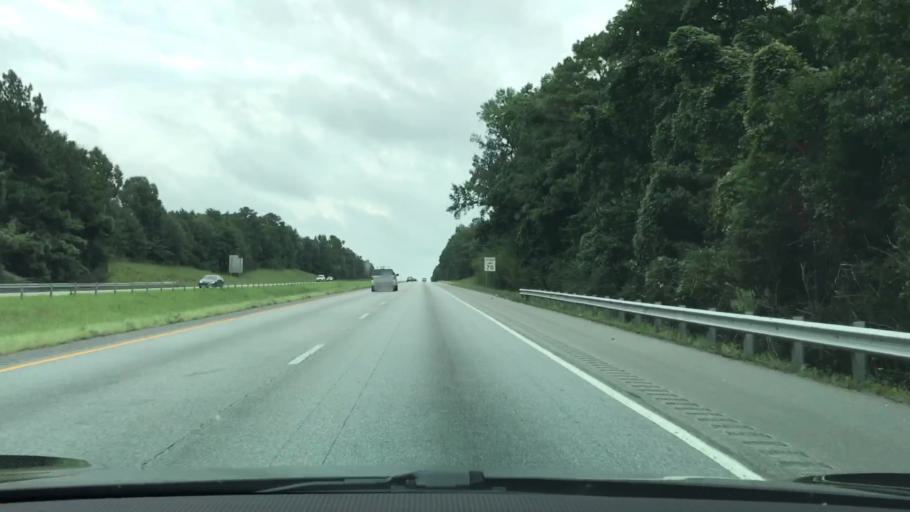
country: US
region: Alabama
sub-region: Lee County
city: Auburn
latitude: 32.5658
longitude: -85.4928
